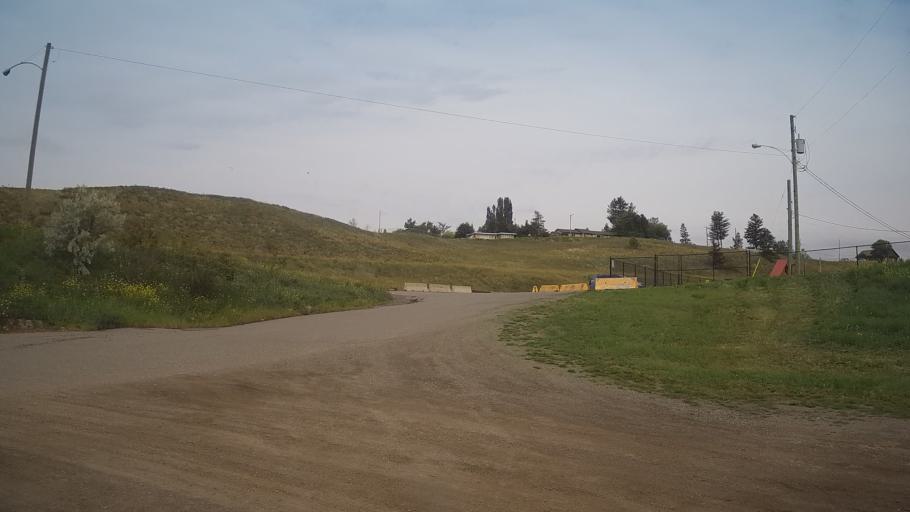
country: CA
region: British Columbia
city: Williams Lake
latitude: 52.1244
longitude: -122.1325
